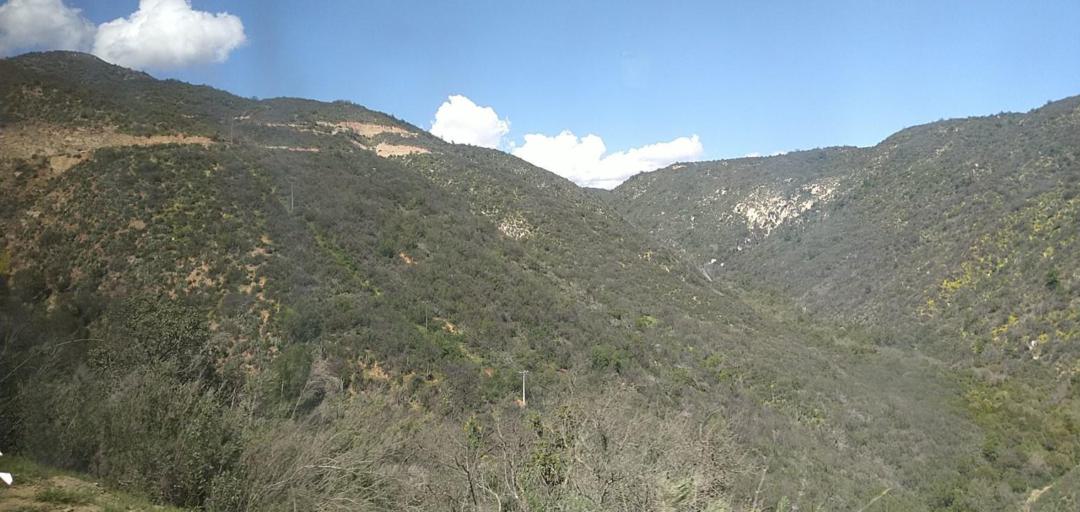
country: CL
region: Valparaiso
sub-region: Provincia de Marga Marga
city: Limache
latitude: -33.2001
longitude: -71.2637
